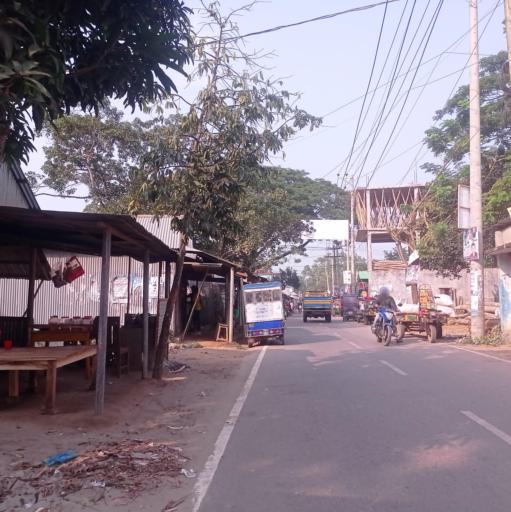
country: BD
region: Dhaka
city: Bhairab Bazar
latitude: 24.0804
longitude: 90.8490
